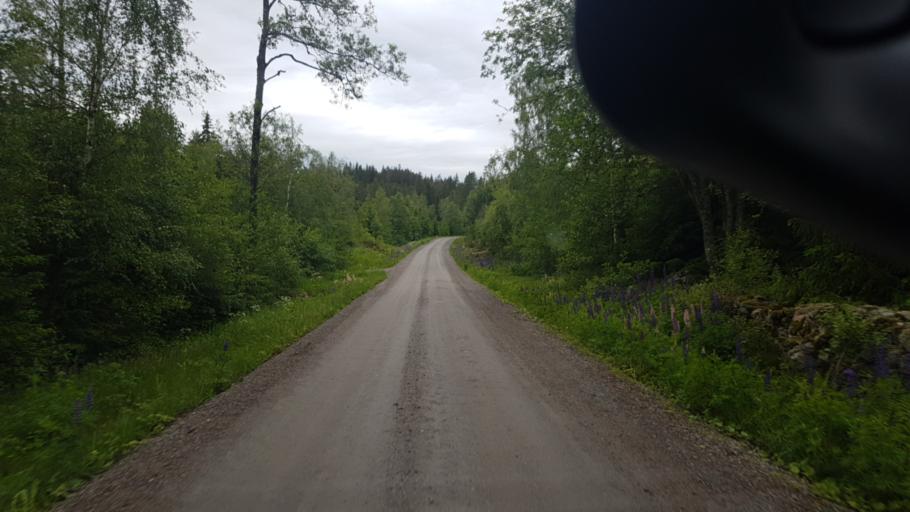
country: NO
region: Ostfold
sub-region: Romskog
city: Romskog
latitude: 59.7049
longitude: 12.0514
